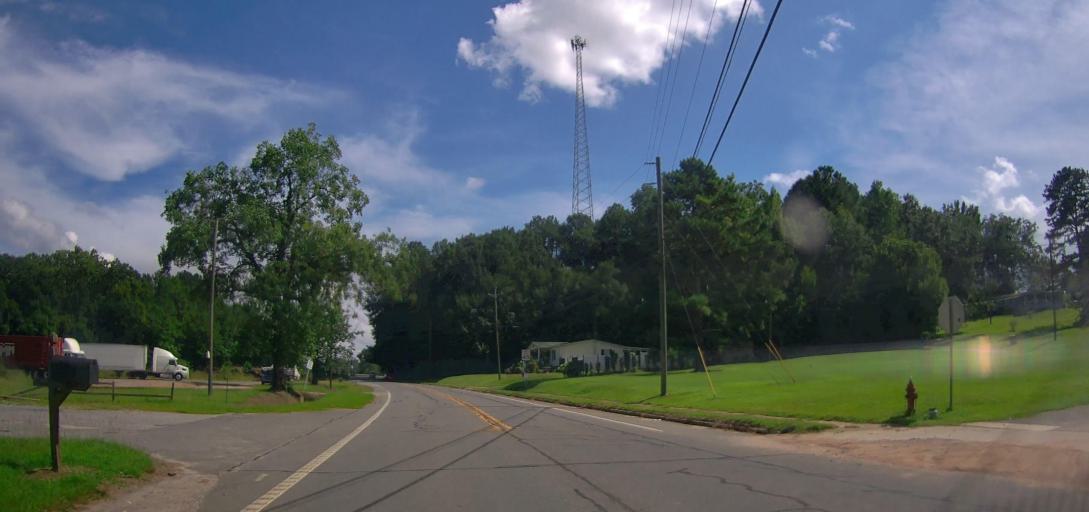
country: US
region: Georgia
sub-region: Talbot County
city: Sardis
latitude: 32.7906
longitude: -84.5640
